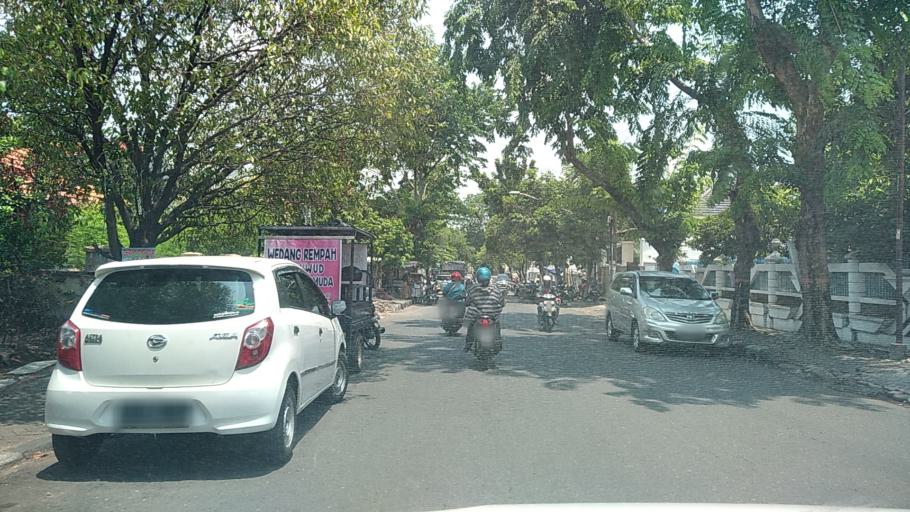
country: ID
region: Central Java
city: Semarang
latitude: -7.0062
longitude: 110.4382
